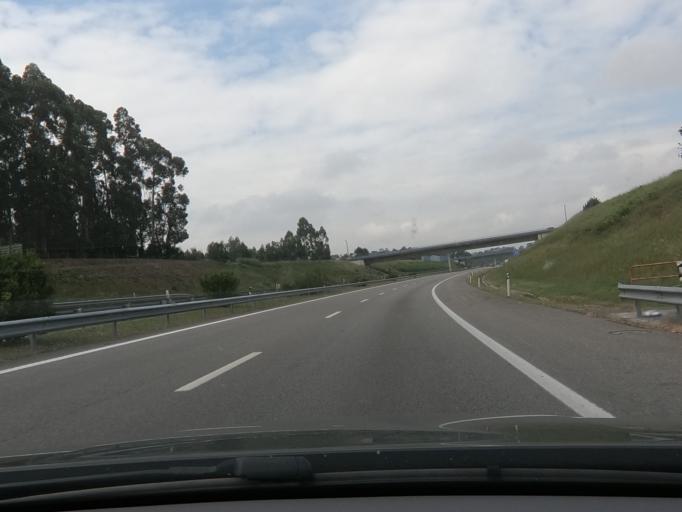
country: PT
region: Aveiro
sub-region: Aveiro
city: Oliveirinha
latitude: 40.6061
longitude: -8.5867
